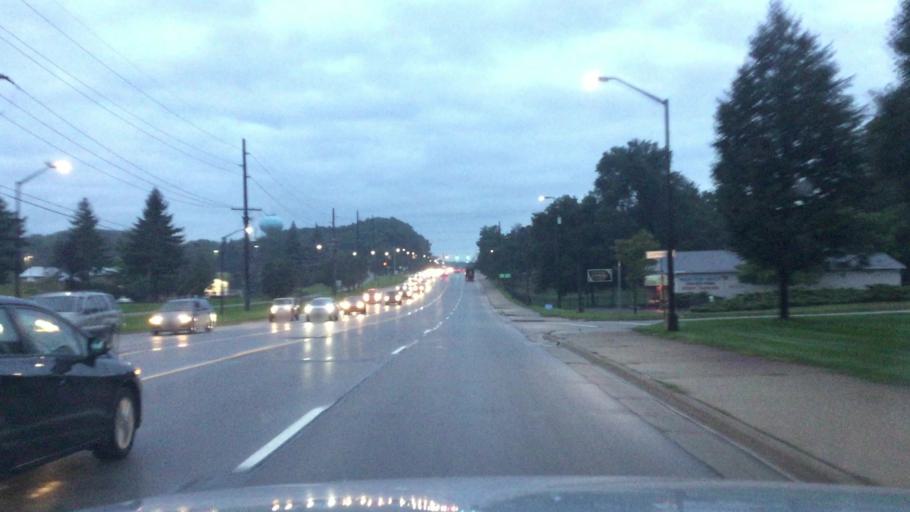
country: US
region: Michigan
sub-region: Oakland County
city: Clarkston
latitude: 42.7241
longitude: -83.4262
